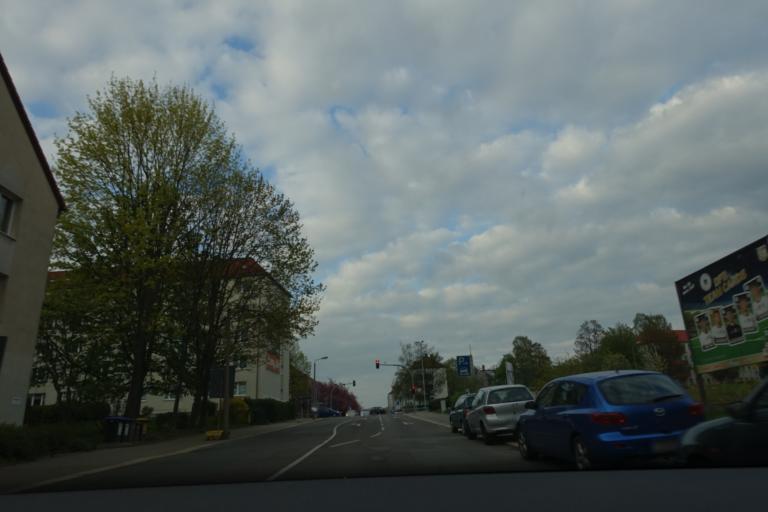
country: DE
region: Saxony
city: Chemnitz
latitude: 50.8231
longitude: 12.9313
